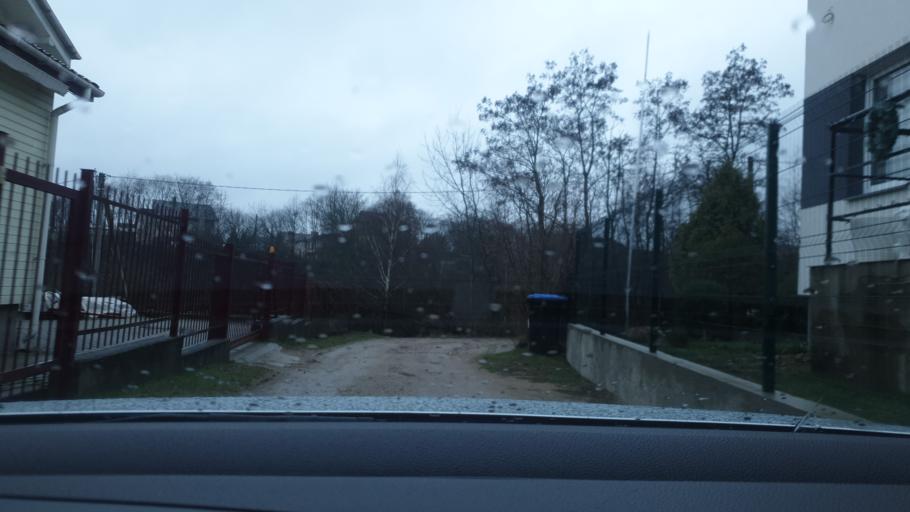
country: LT
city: Skaidiskes
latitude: 54.7025
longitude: 25.4048
